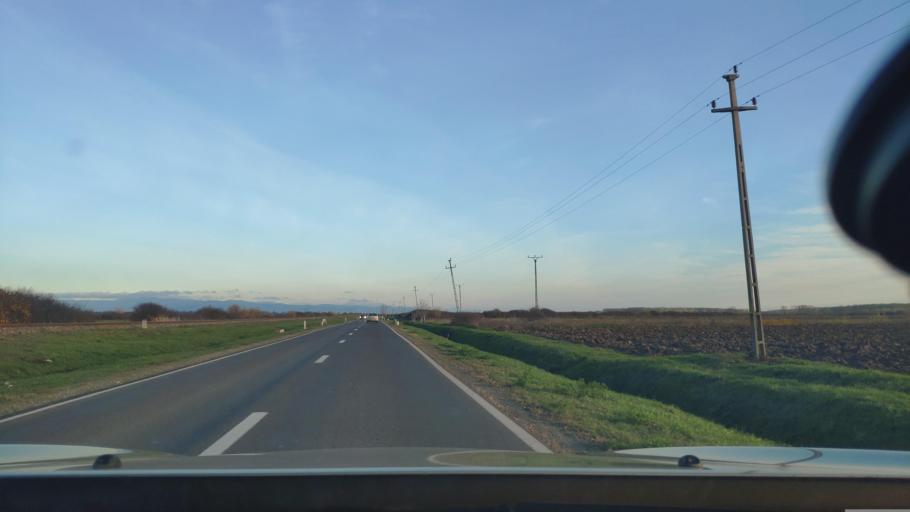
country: RO
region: Satu Mare
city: Culciu Mic
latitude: 47.7901
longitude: 23.0397
